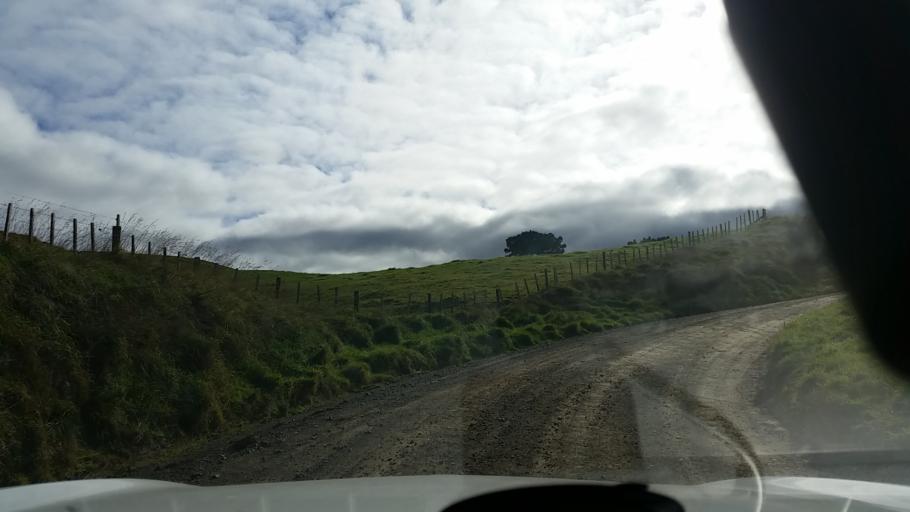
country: NZ
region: Hawke's Bay
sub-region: Napier City
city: Napier
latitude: -39.1131
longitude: 176.8959
